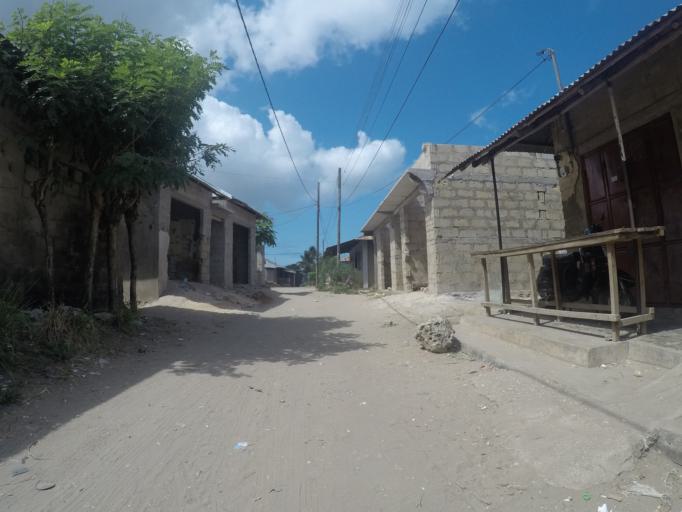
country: TZ
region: Zanzibar Urban/West
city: Zanzibar
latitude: -6.1806
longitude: 39.2122
